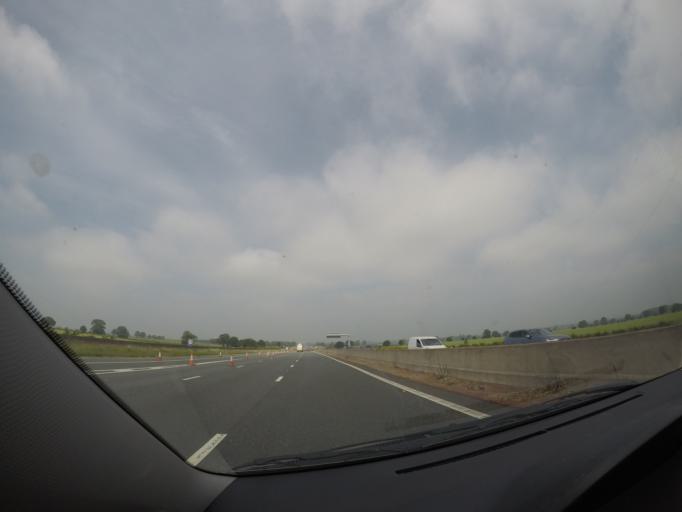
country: GB
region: England
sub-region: North Yorkshire
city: Ripon
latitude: 54.1854
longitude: -1.4605
